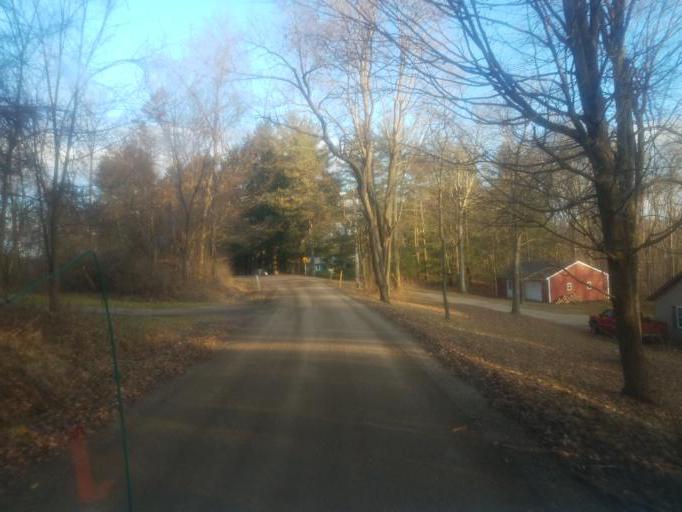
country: US
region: Ohio
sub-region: Sandusky County
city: Bellville
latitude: 40.5782
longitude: -82.4461
